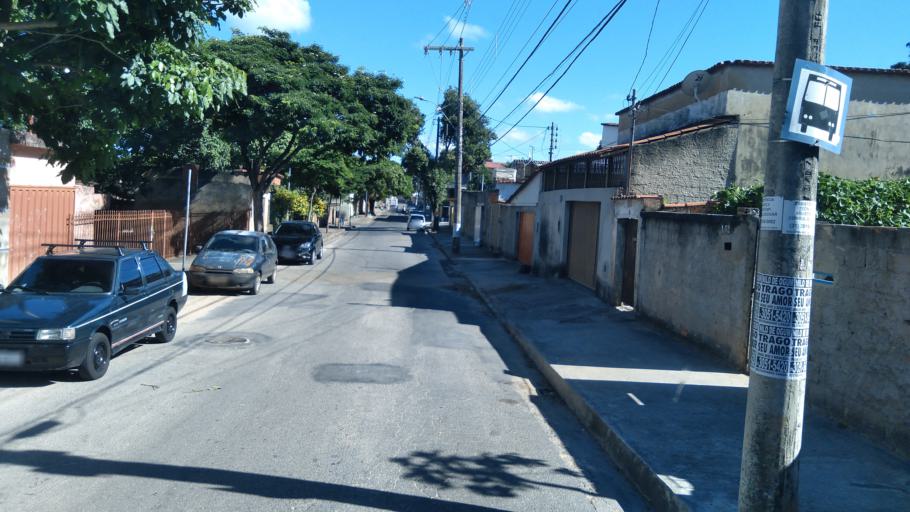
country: BR
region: Minas Gerais
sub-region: Belo Horizonte
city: Belo Horizonte
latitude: -19.8553
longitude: -43.9118
